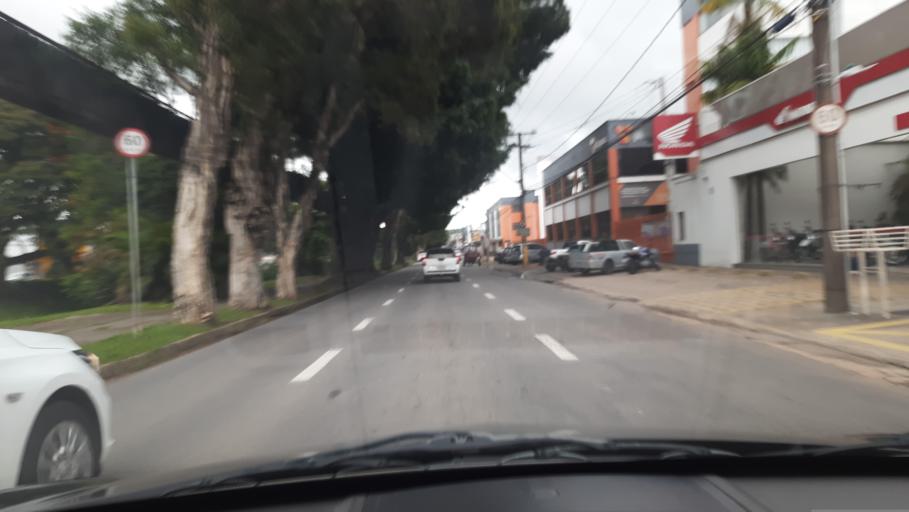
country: BR
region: Minas Gerais
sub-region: Pocos De Caldas
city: Pocos de Caldas
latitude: -21.7853
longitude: -46.5821
